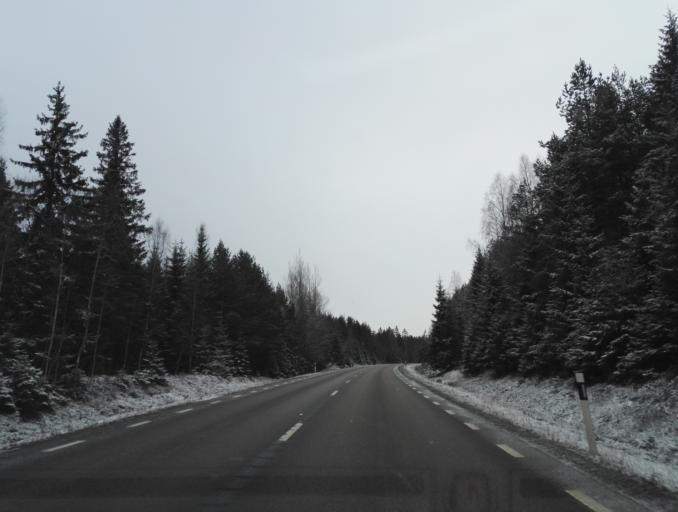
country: SE
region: Kronoberg
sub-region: Uppvidinge Kommun
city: Aseda
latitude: 57.1724
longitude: 15.4947
